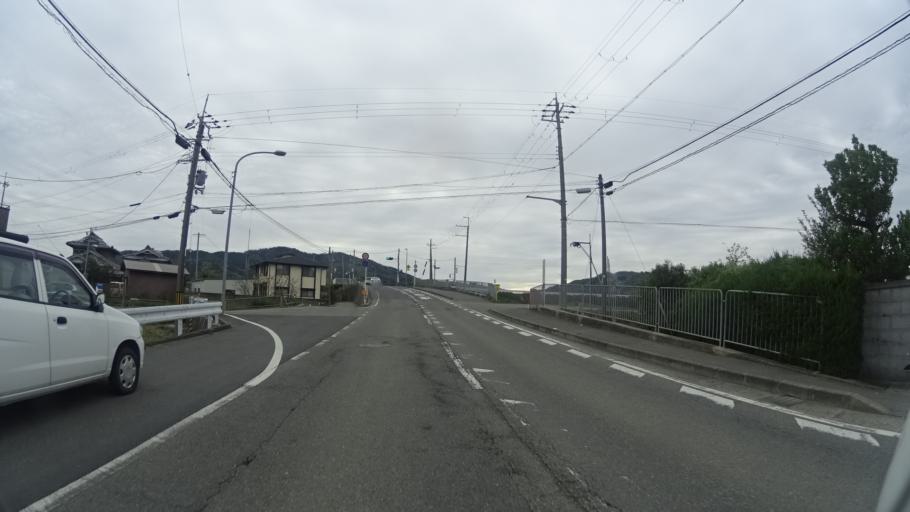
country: JP
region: Kyoto
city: Kameoka
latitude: 35.0521
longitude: 135.5535
